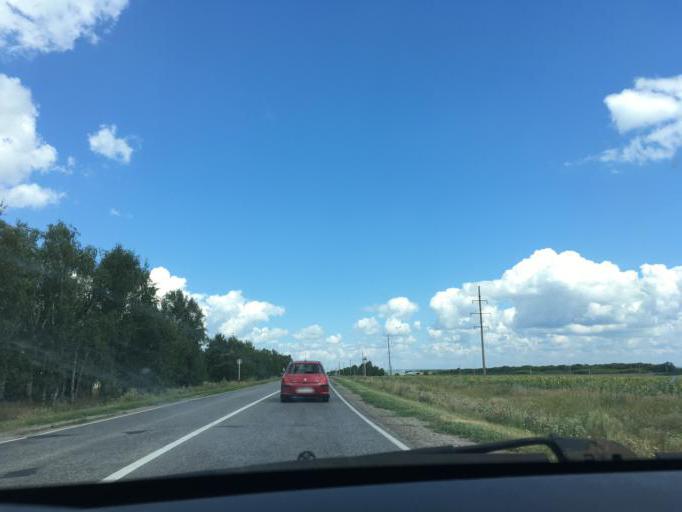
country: RU
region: Samara
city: Bezenchuk
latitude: 53.0402
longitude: 49.4410
